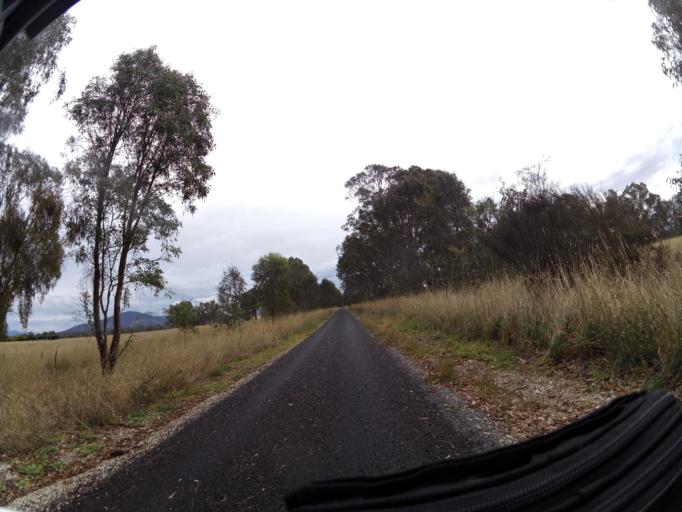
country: AU
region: New South Wales
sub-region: Albury Municipality
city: East Albury
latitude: -36.1400
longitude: 146.9837
